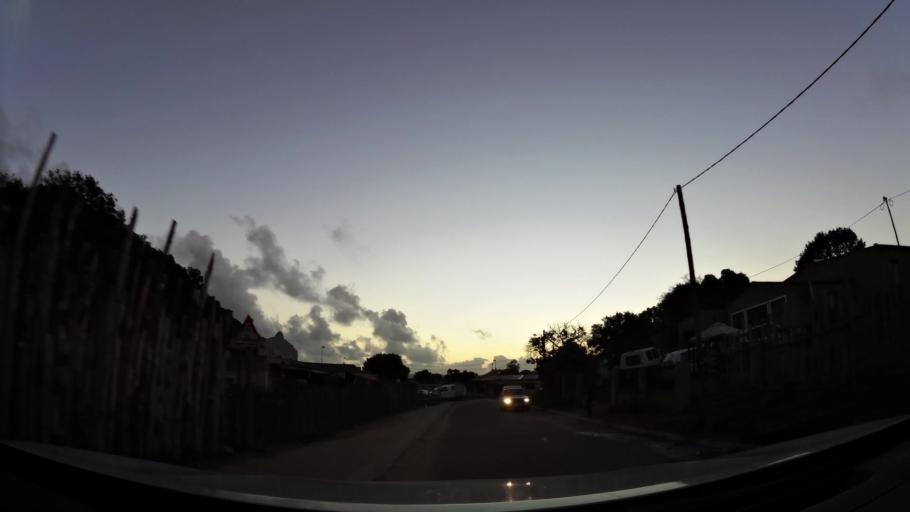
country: ZA
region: Western Cape
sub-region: Eden District Municipality
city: Knysna
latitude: -34.0275
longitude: 22.8202
